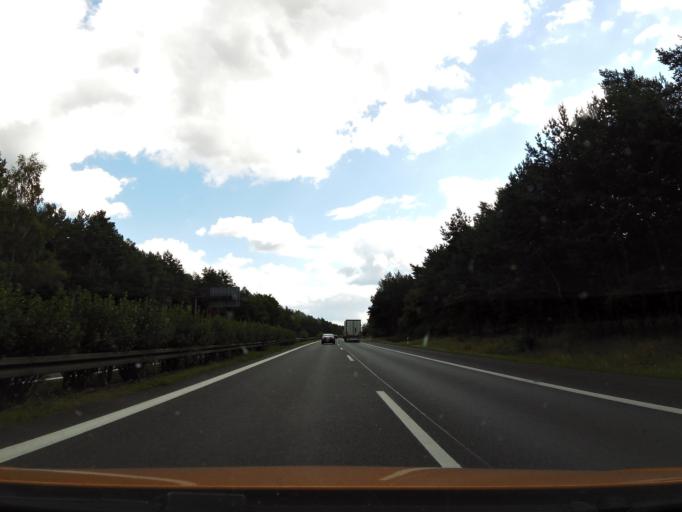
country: DE
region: Brandenburg
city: Birkenwerder
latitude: 52.6976
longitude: 13.2941
